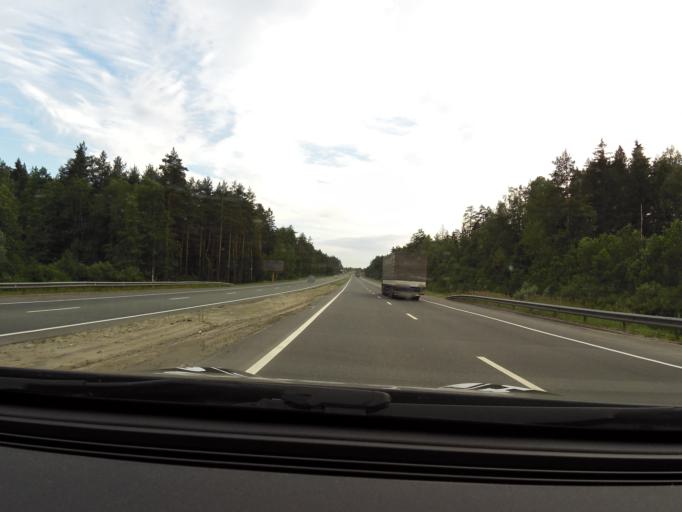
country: RU
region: Vladimir
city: Kommunar
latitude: 56.0733
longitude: 40.4663
